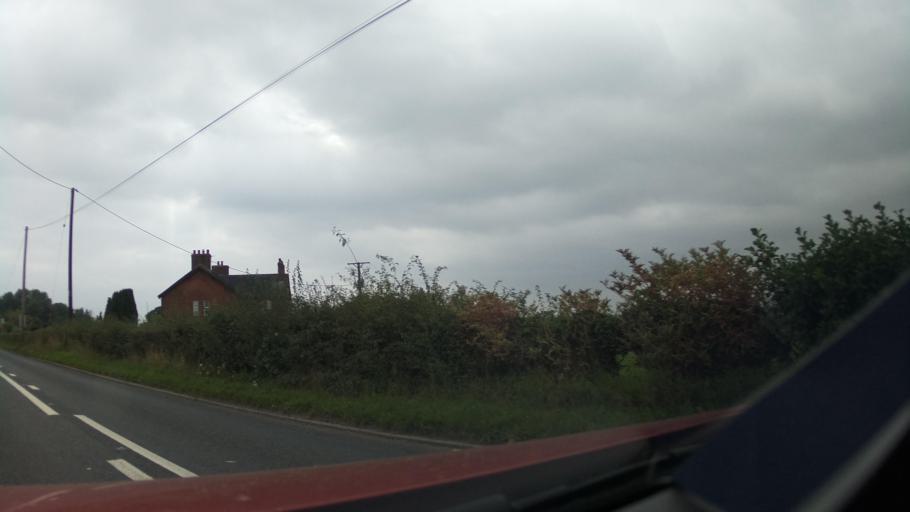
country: GB
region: England
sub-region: Staffordshire
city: Cheadle
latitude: 53.0173
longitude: -2.0111
